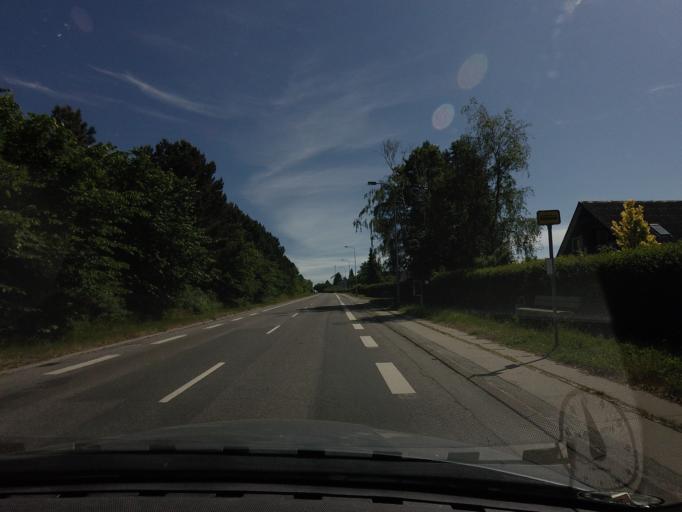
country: DK
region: Central Jutland
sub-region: Norddjurs Kommune
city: Grenaa
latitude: 56.4247
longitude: 10.8614
